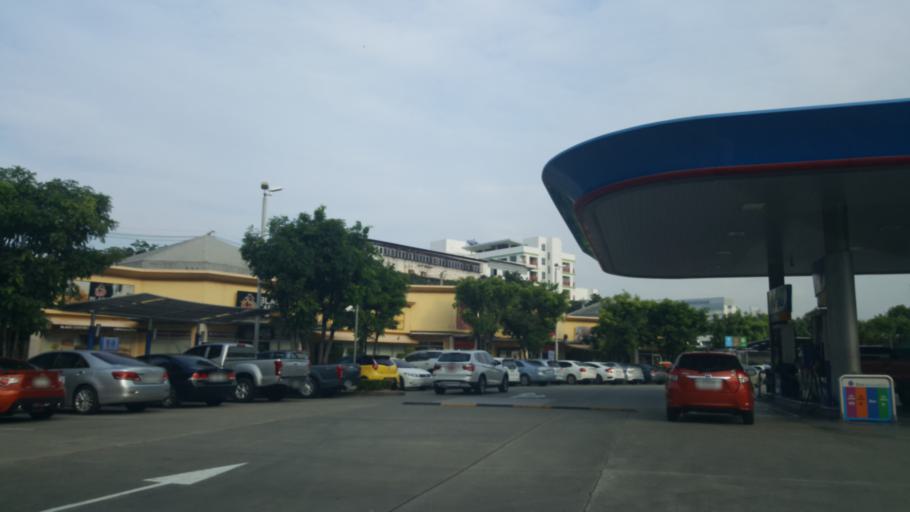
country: TH
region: Bangkok
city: Phra Khanong
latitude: 13.6865
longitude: 100.6030
